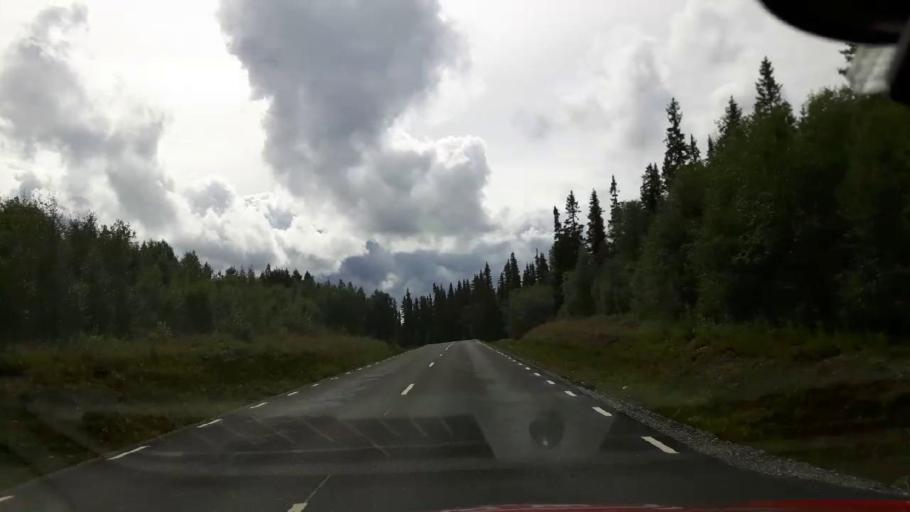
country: NO
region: Nord-Trondelag
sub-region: Lierne
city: Sandvika
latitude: 64.6118
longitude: 14.1194
